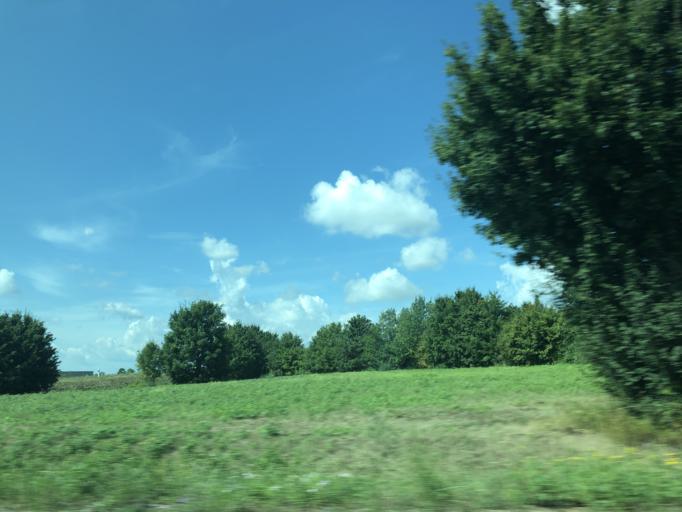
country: DE
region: Rheinland-Pfalz
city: Rulzheim
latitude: 49.1694
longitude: 8.3024
